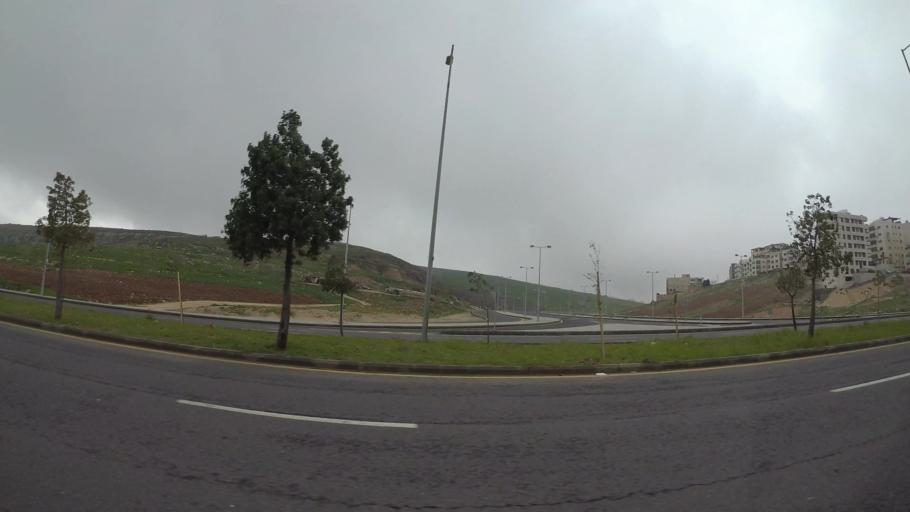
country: JO
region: Amman
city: Al Bunayyat ash Shamaliyah
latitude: 31.9349
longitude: 35.8738
